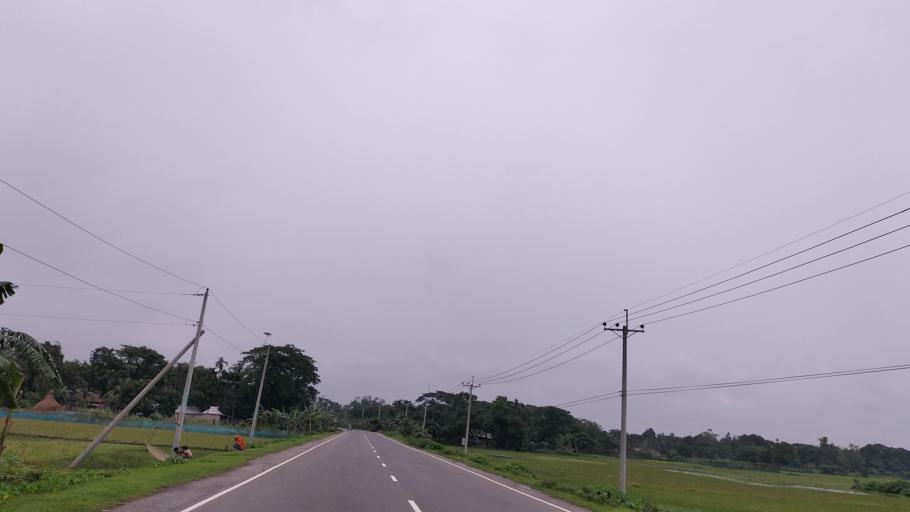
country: BD
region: Dhaka
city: Netrakona
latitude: 24.8519
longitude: 90.6208
